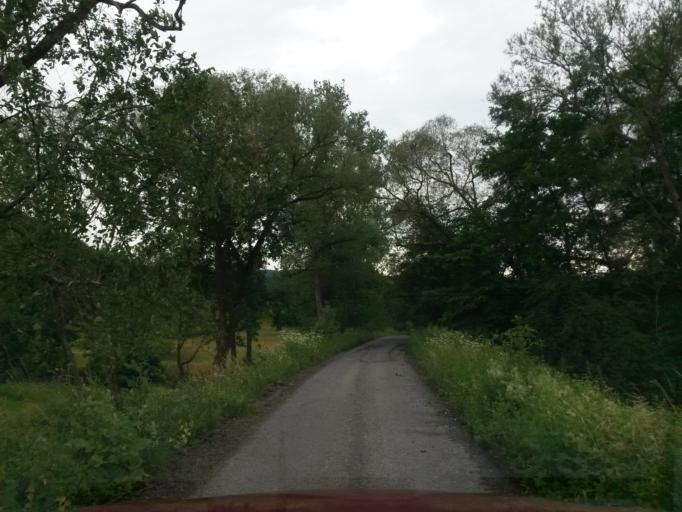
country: SK
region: Banskobystricky
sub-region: Okres Banska Bystrica
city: Zvolen
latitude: 48.5565
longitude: 19.2349
